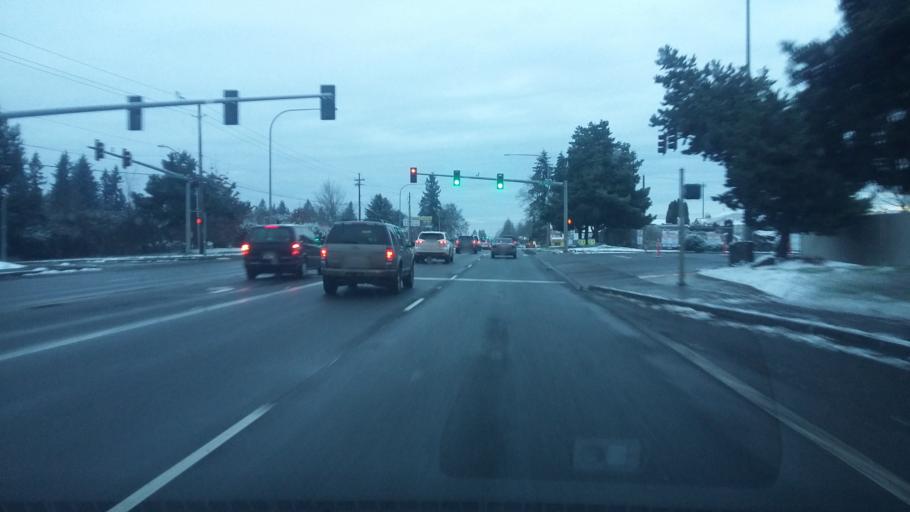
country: US
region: Washington
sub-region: Clark County
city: Orchards
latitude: 45.6851
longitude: -122.5525
